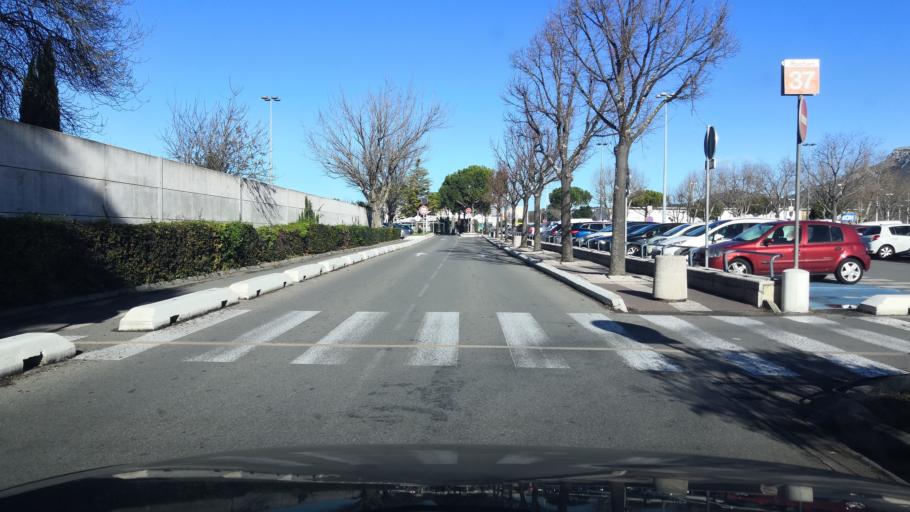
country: FR
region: Provence-Alpes-Cote d'Azur
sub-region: Departement des Bouches-du-Rhone
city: Aubagne
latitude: 43.2953
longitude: 5.5919
